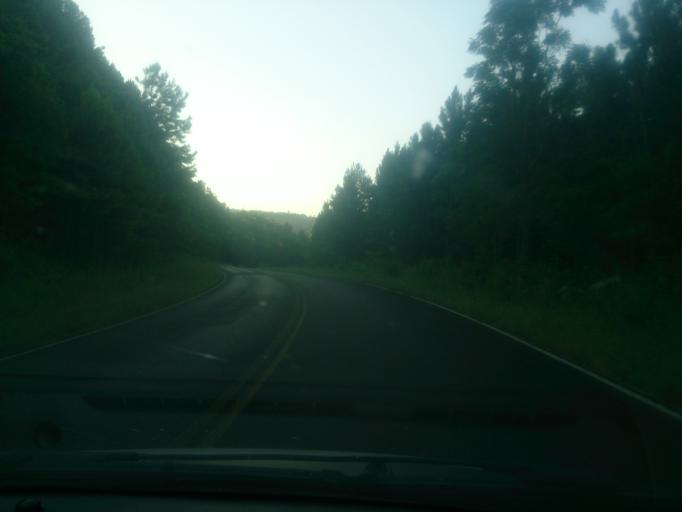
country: AR
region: Misiones
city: Panambi
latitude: -27.6742
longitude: -54.9109
